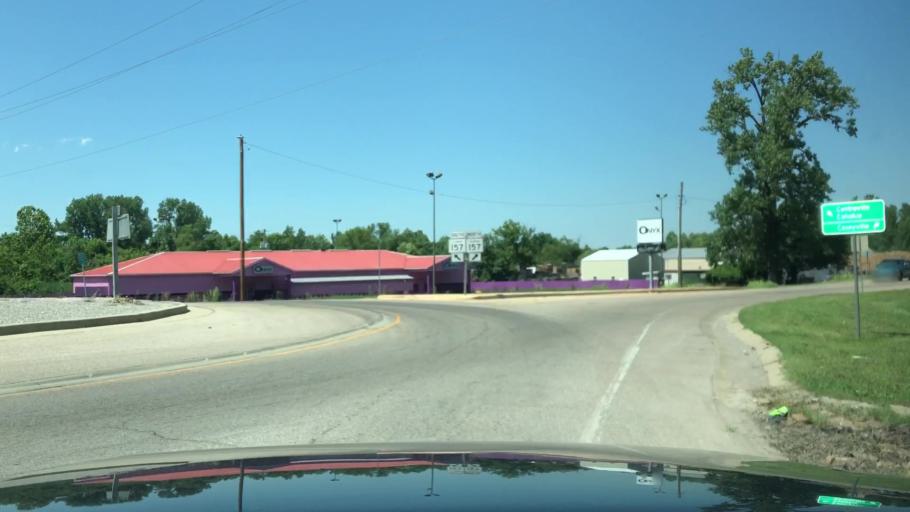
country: US
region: Illinois
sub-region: Saint Clair County
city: Centreville
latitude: 38.5586
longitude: -90.0994
